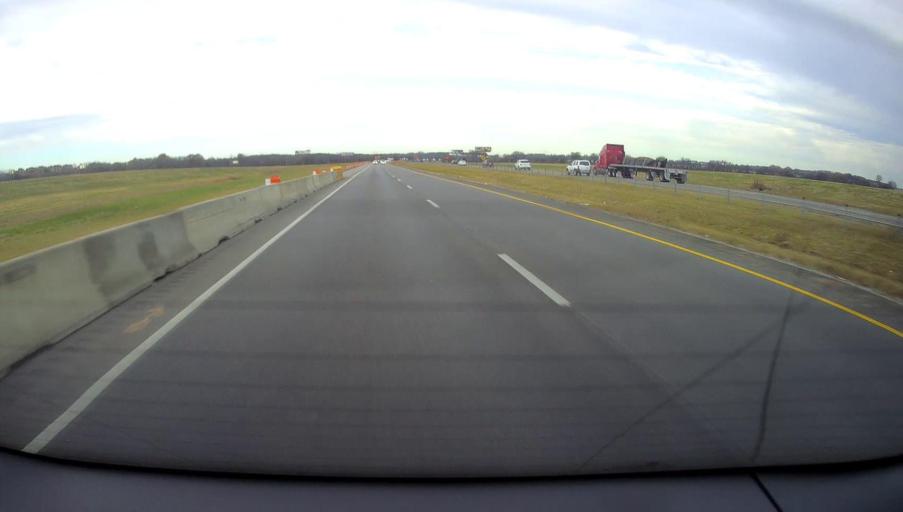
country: US
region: Alabama
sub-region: Limestone County
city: Athens
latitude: 34.7319
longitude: -86.9362
